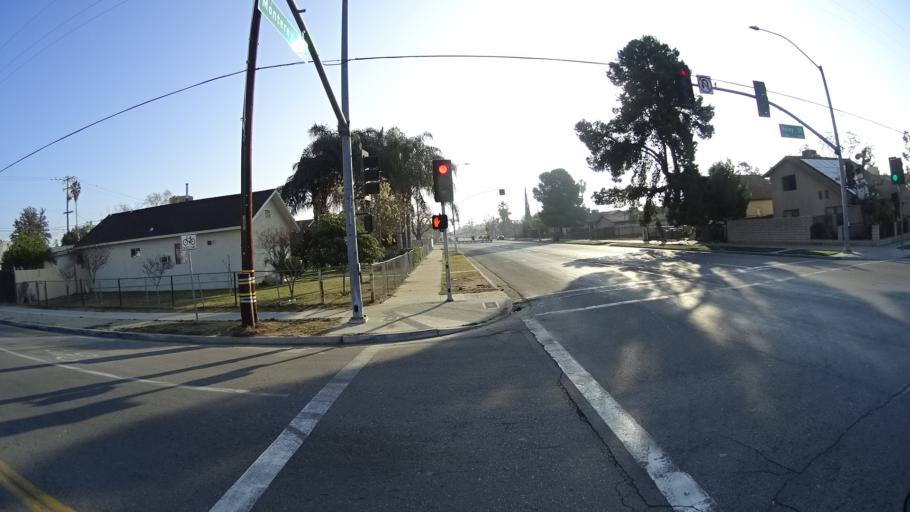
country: US
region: California
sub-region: Kern County
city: Bakersfield
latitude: 35.3785
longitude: -118.9806
